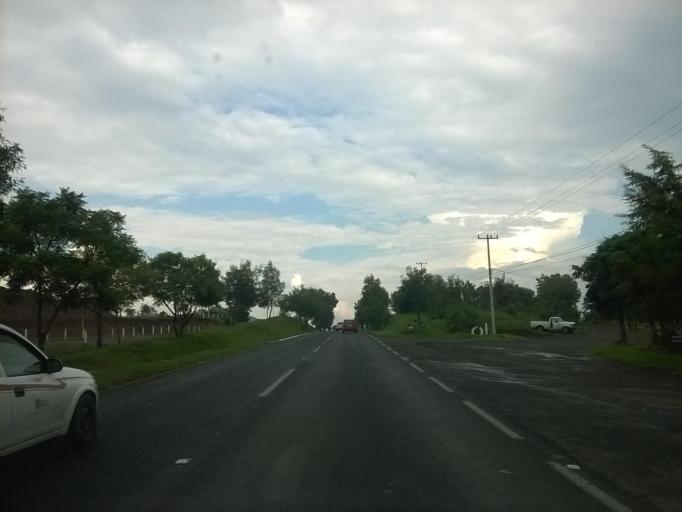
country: MX
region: Michoacan
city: Cuanajo
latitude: 19.5347
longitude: -101.5073
